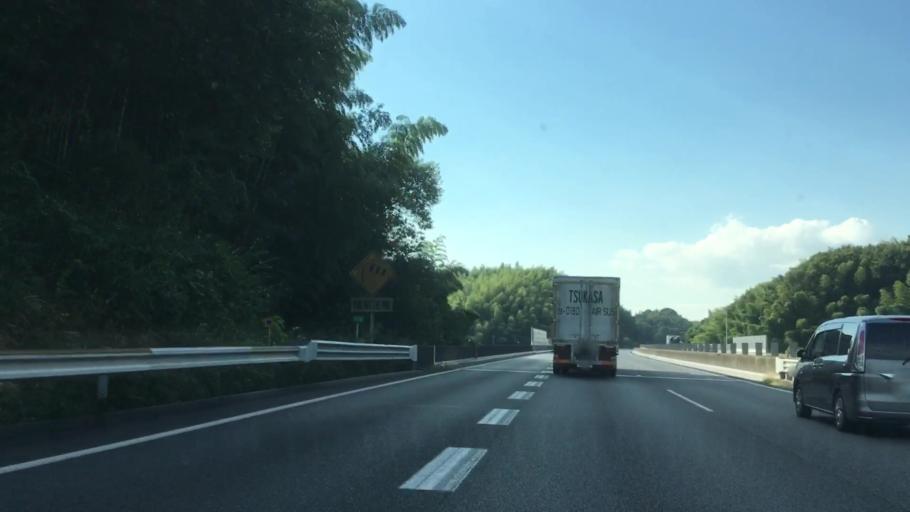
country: JP
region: Yamaguchi
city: Kudamatsu
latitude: 34.0312
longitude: 131.9366
